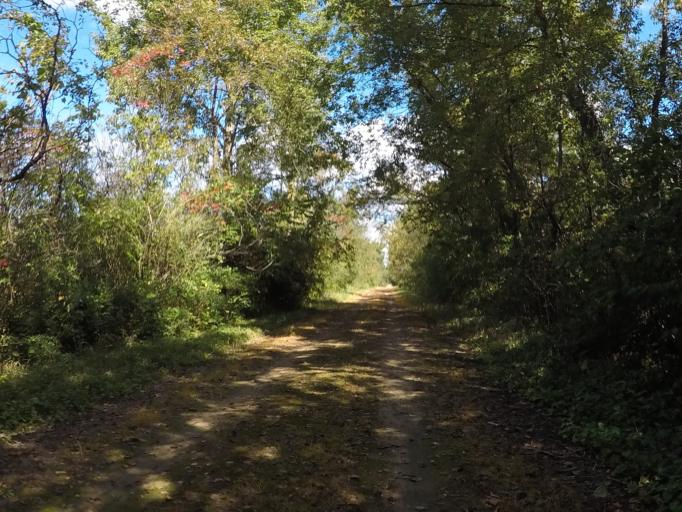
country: US
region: Wisconsin
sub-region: Richland County
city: Richland Center
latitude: 43.2497
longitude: -90.3043
